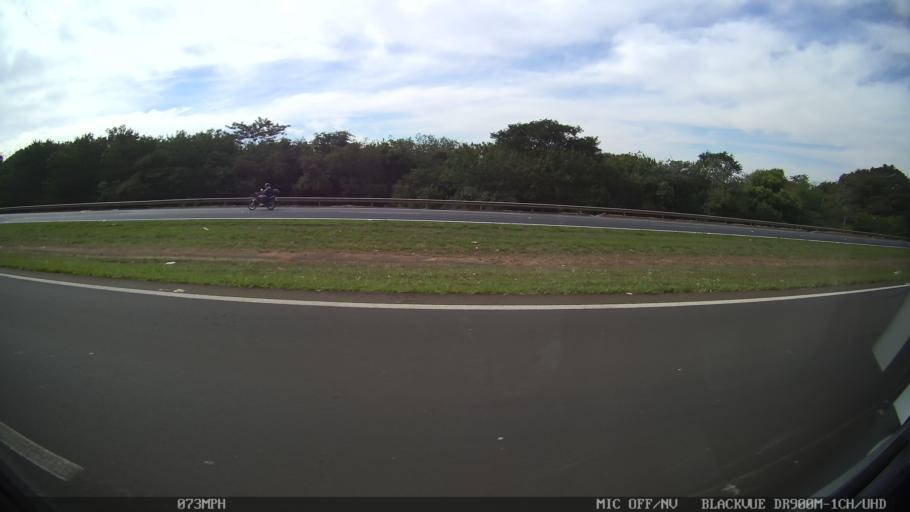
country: BR
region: Sao Paulo
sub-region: Matao
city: Matao
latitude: -21.5858
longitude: -48.4473
